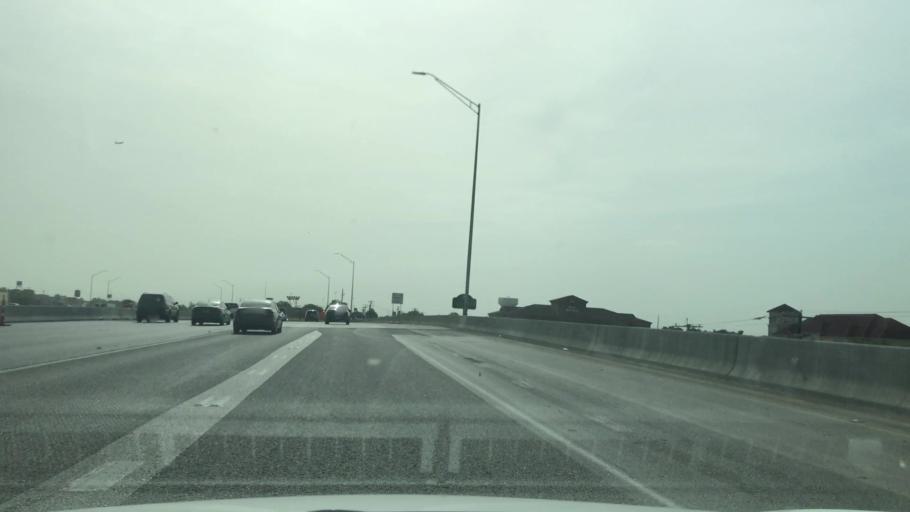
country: US
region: Texas
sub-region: Tarrant County
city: Euless
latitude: 32.8373
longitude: -97.0918
